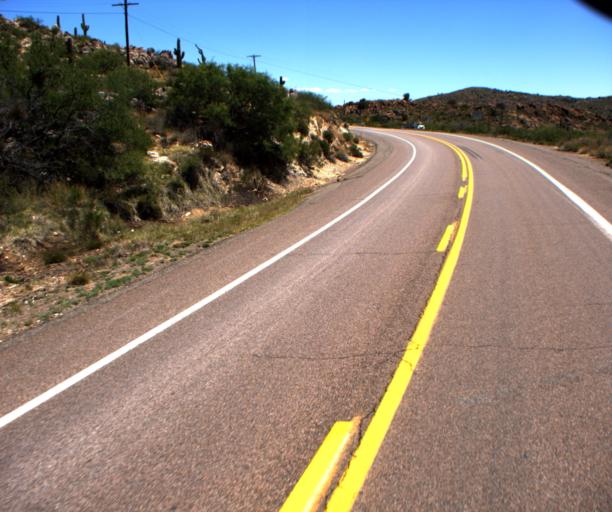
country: US
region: Arizona
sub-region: Yavapai County
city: Bagdad
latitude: 34.5274
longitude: -113.1349
